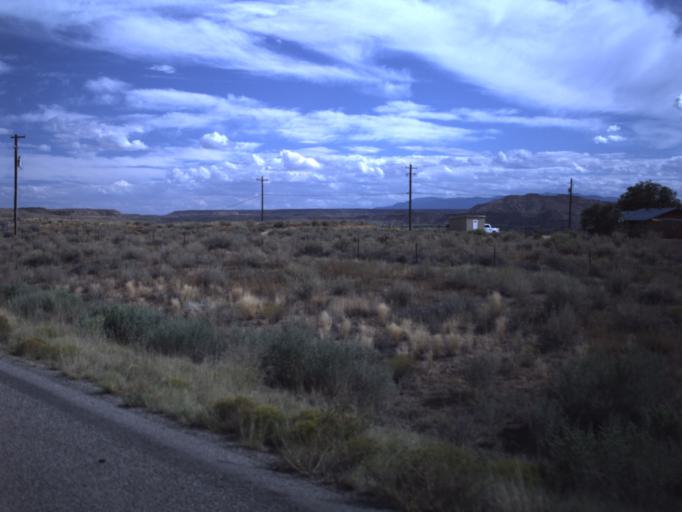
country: US
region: Colorado
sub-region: Montezuma County
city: Towaoc
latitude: 37.2067
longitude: -109.1640
